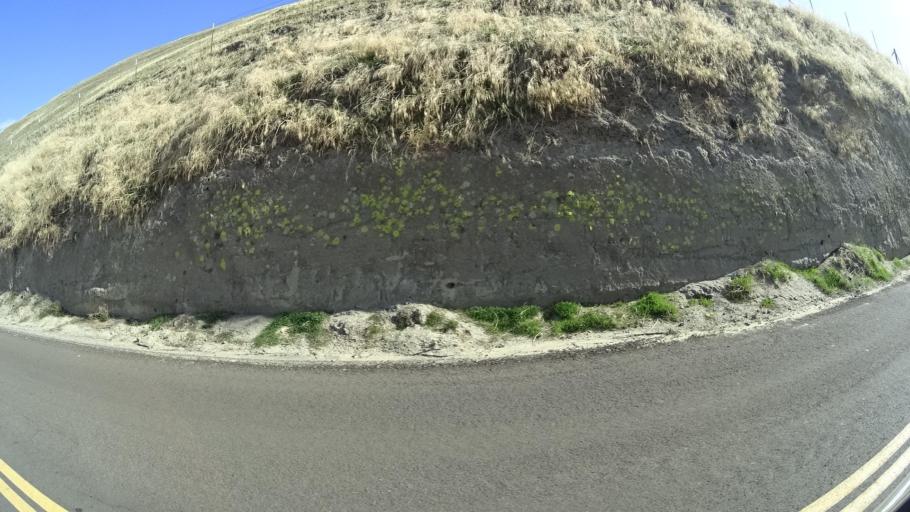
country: US
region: California
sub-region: Tulare County
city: Richgrove
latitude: 35.6676
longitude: -118.9150
